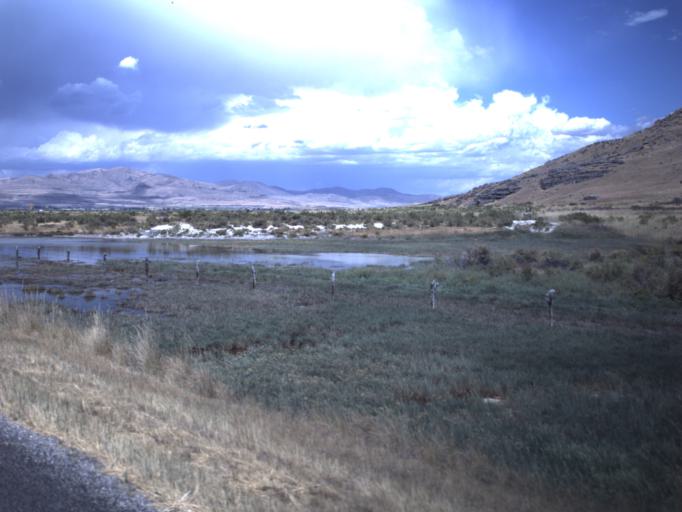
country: US
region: Utah
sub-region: Box Elder County
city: Elwood
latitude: 41.5820
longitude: -112.2572
